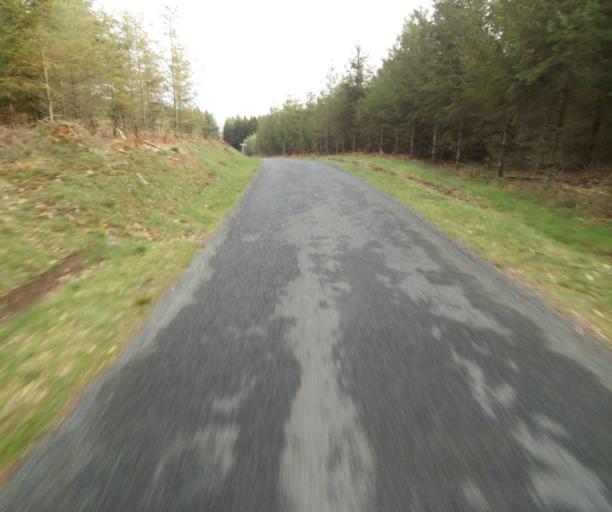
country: FR
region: Limousin
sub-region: Departement de la Correze
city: Argentat
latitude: 45.2178
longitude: 1.9402
